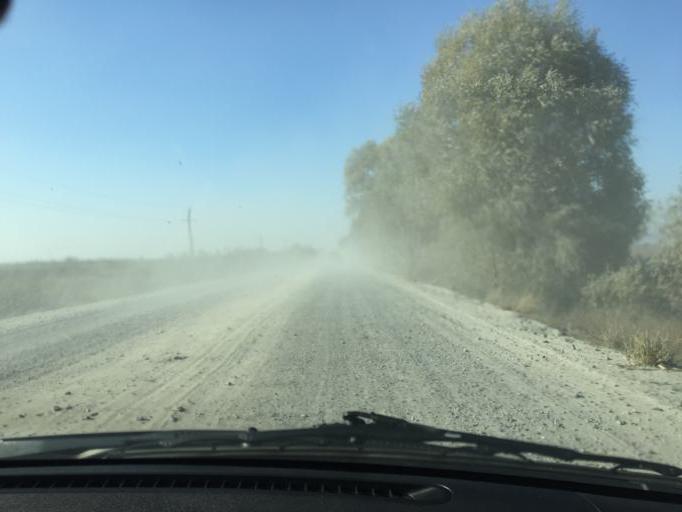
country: BY
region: Gomel
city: Turaw
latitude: 52.0689
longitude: 27.8190
